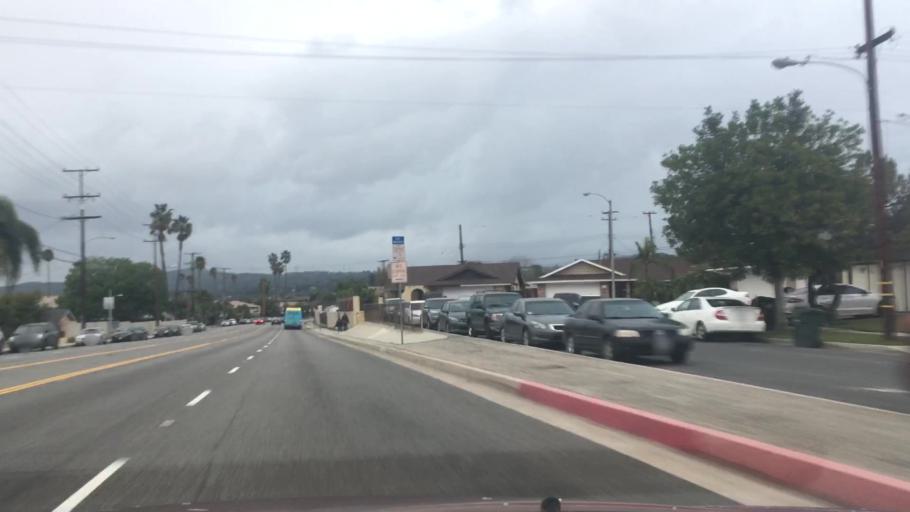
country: US
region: California
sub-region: Los Angeles County
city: East La Mirada
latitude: 33.9256
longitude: -117.9944
